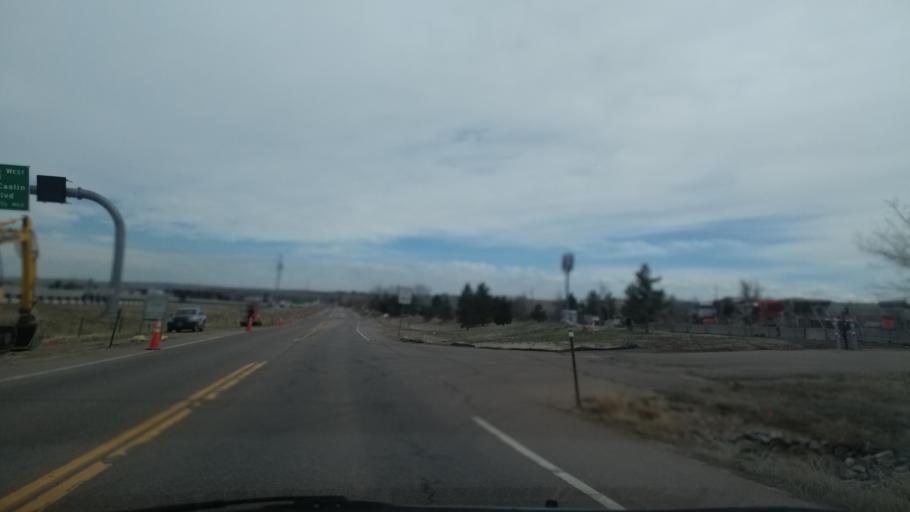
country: US
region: Colorado
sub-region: Boulder County
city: Superior
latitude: 39.9617
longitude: -105.1771
